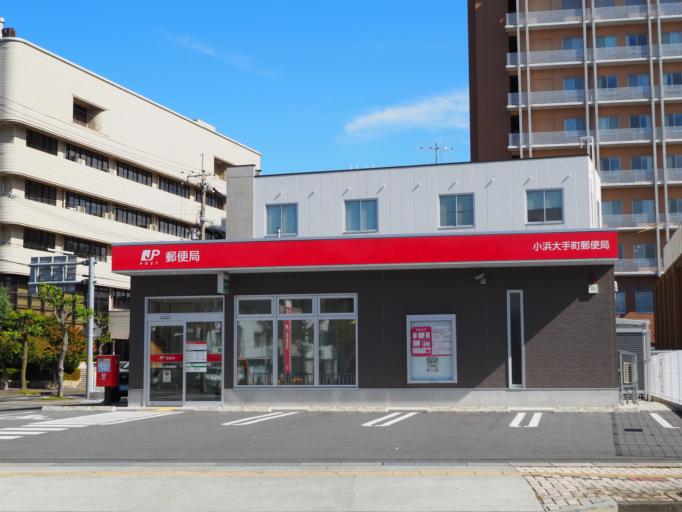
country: JP
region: Fukui
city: Obama
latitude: 35.4952
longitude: 135.7455
